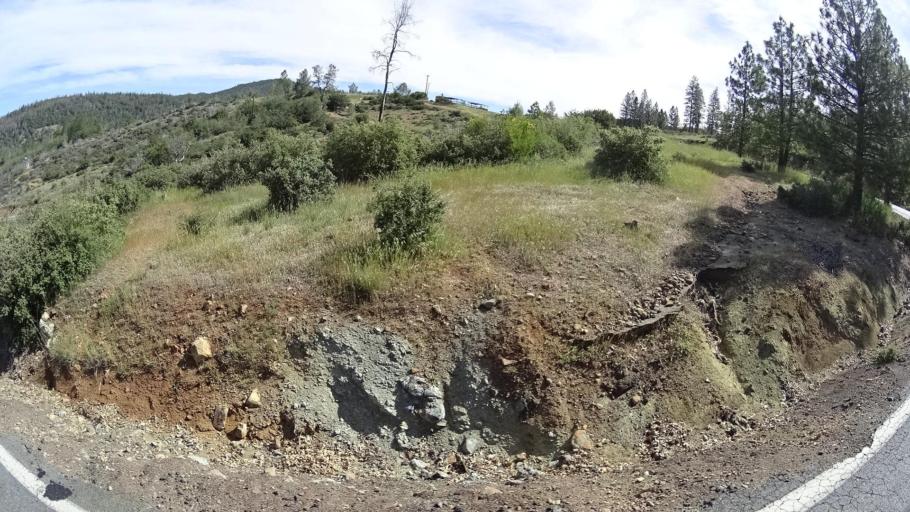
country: US
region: California
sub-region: Lake County
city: Cobb
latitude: 38.8559
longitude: -122.7537
